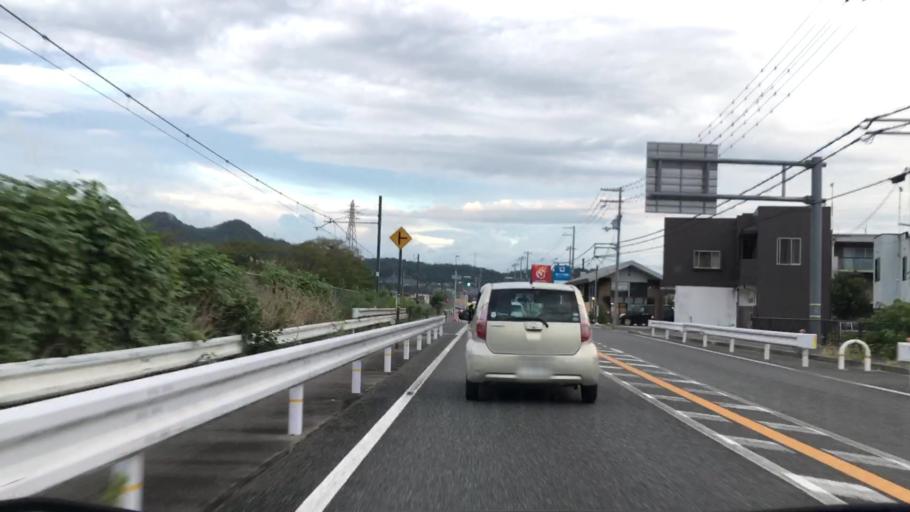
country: JP
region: Hyogo
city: Himeji
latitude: 34.8762
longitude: 134.7293
